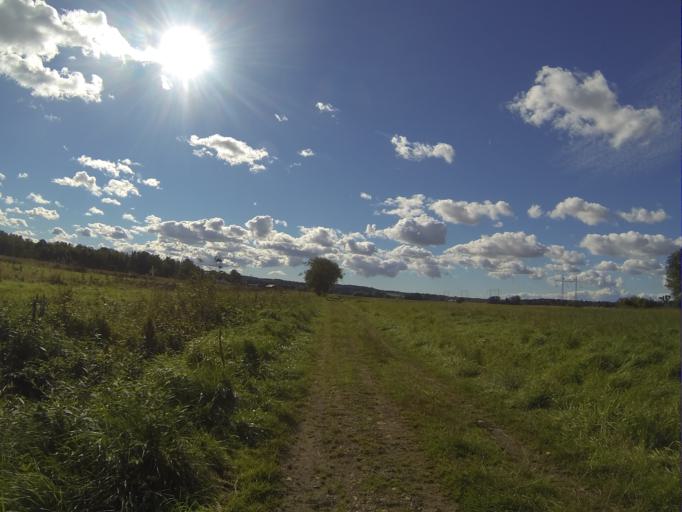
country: SE
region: Skane
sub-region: Hoors Kommun
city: Loberod
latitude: 55.7262
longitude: 13.3911
